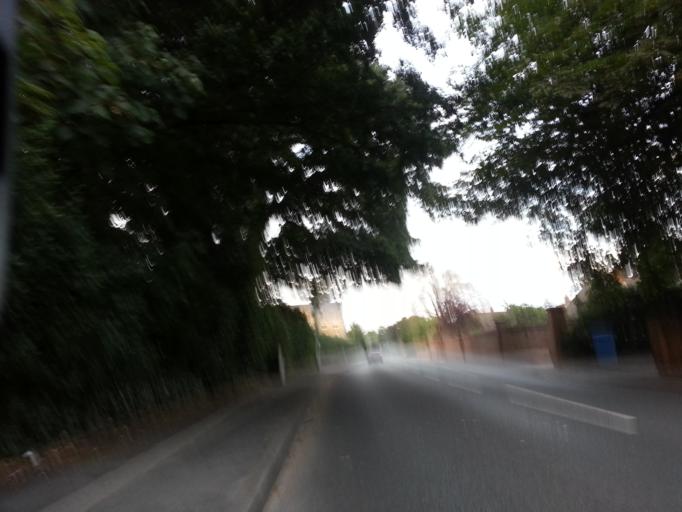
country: GB
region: England
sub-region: Suffolk
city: Ipswich
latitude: 52.0452
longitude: 1.1394
